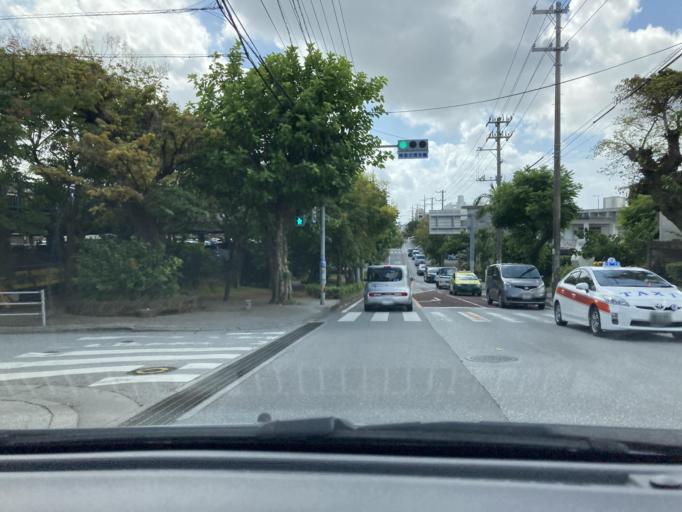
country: JP
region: Okinawa
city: Ginowan
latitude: 26.2557
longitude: 127.7221
